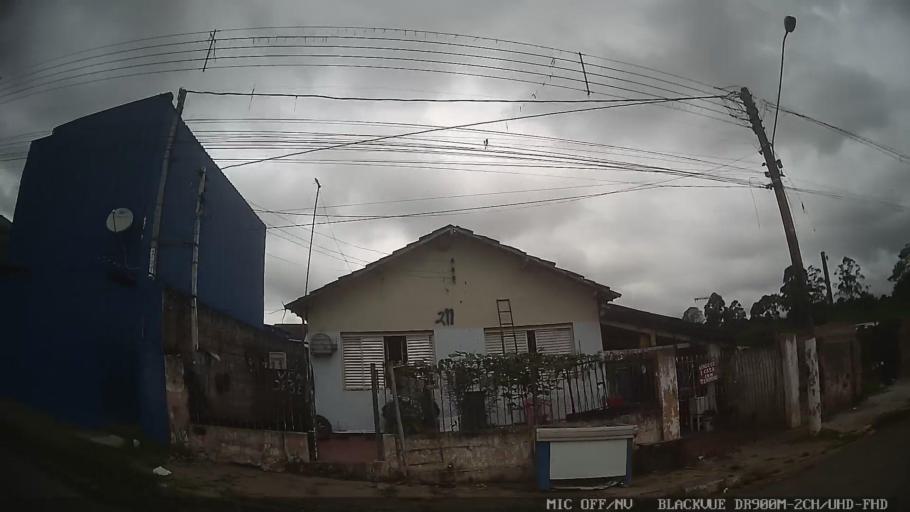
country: BR
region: Sao Paulo
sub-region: Atibaia
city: Atibaia
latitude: -23.1189
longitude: -46.5887
